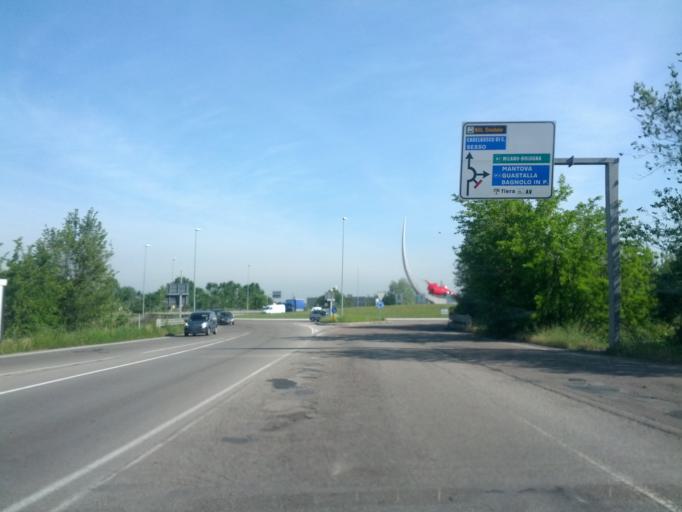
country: IT
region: Emilia-Romagna
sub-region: Provincia di Reggio Emilia
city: Reggio nell'Emilia
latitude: 44.7204
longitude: 10.6241
